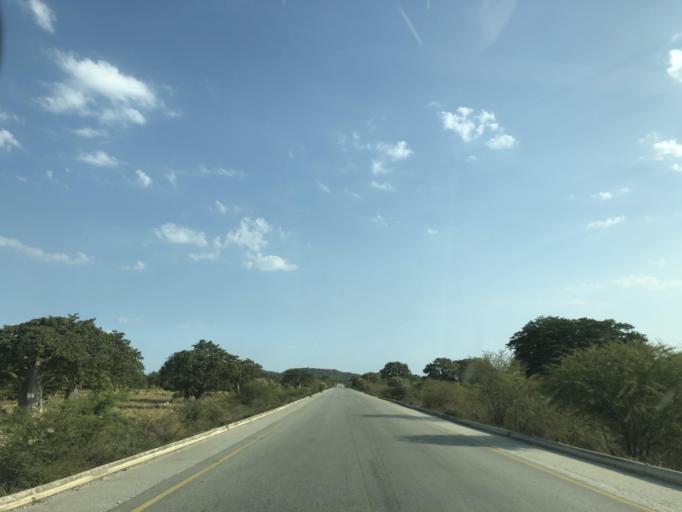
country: AO
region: Benguela
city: Benguela
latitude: -13.2315
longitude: 13.7698
